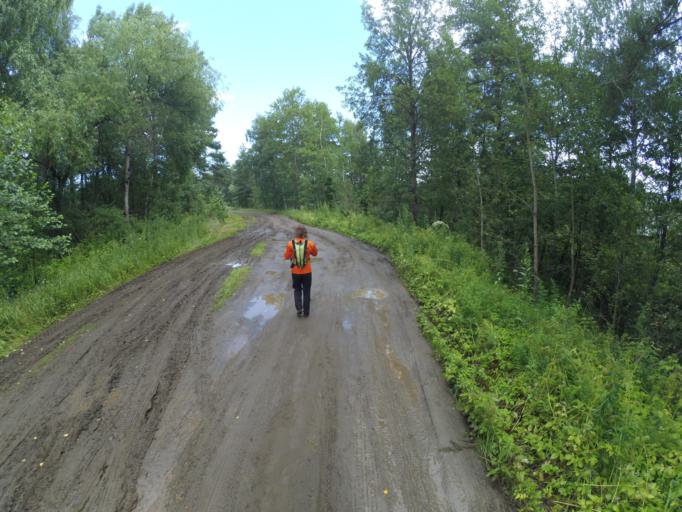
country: RU
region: Moskovskaya
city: Fosforitnyy
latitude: 55.3315
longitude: 38.9139
